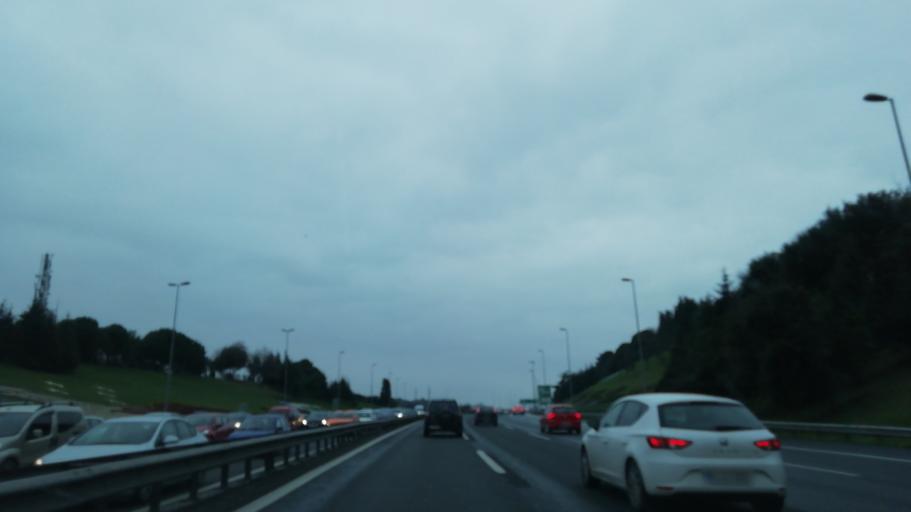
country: TR
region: Istanbul
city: UEskuedar
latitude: 41.0332
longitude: 29.0451
